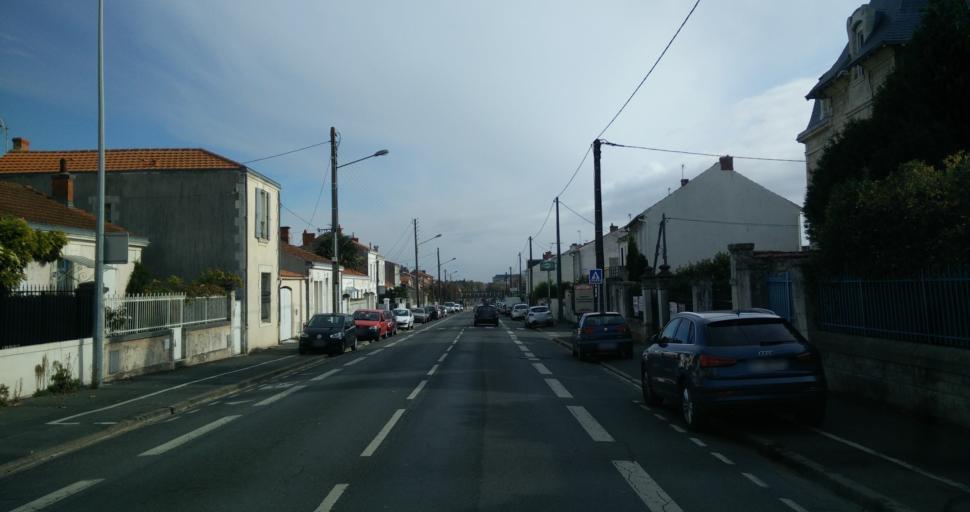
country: FR
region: Poitou-Charentes
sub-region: Departement de la Charente-Maritime
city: La Rochelle
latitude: 46.1640
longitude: -1.1743
